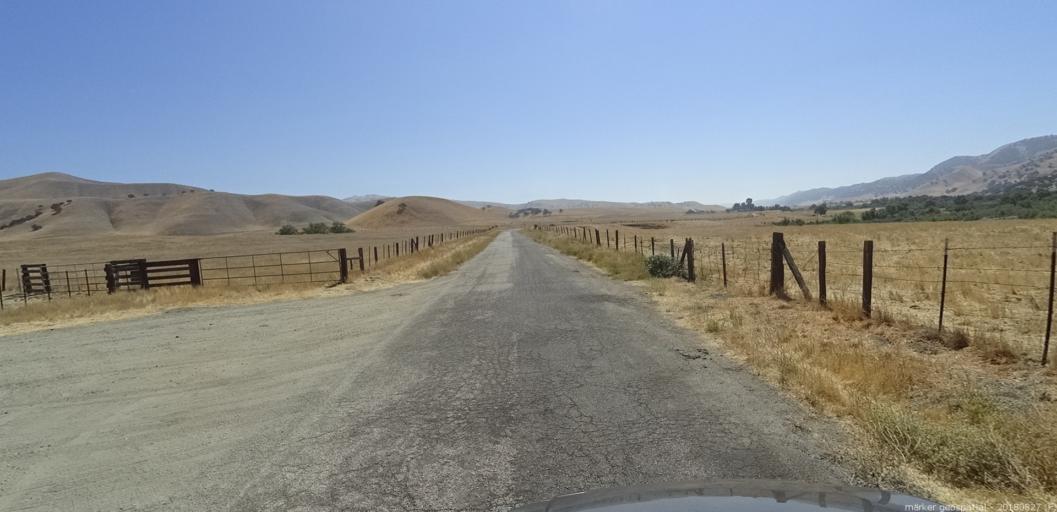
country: US
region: California
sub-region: Monterey County
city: King City
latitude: 36.2907
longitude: -120.9698
